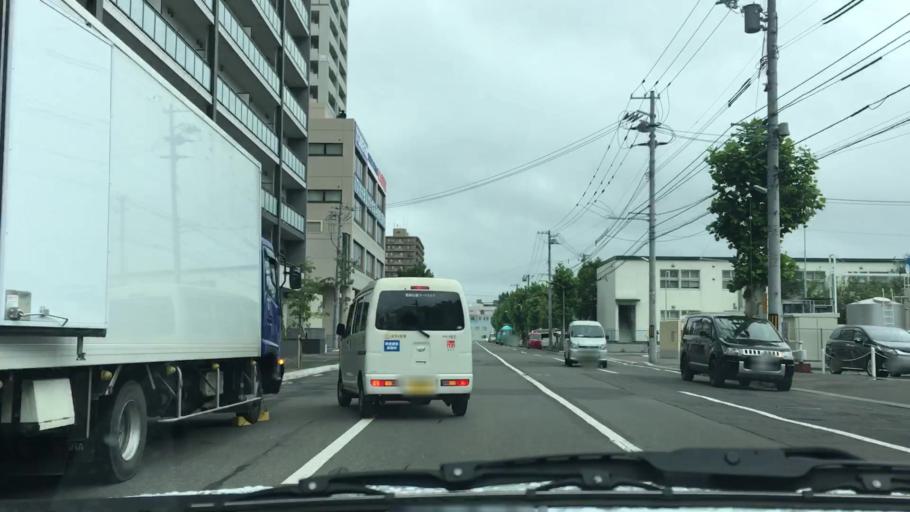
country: JP
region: Hokkaido
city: Sapporo
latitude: 43.0695
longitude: 141.3620
